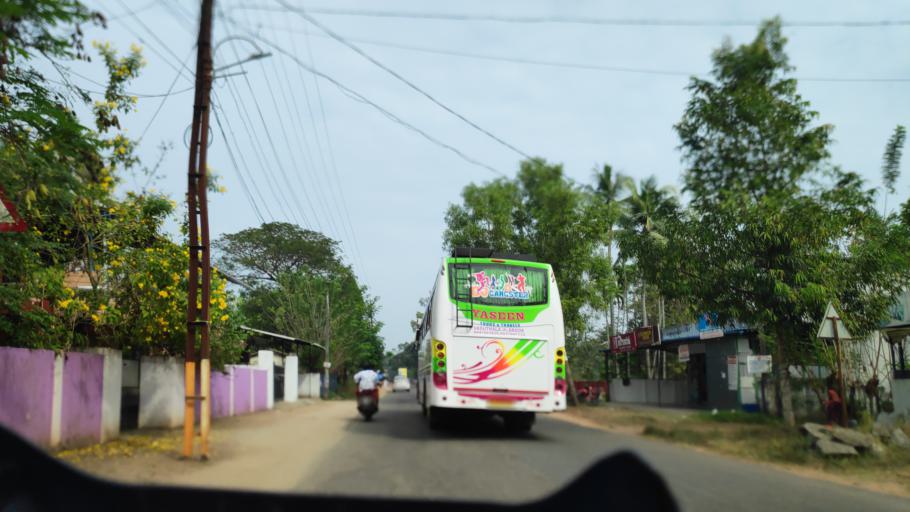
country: IN
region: Kerala
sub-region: Alappuzha
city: Kutiatodu
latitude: 9.8174
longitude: 76.3511
